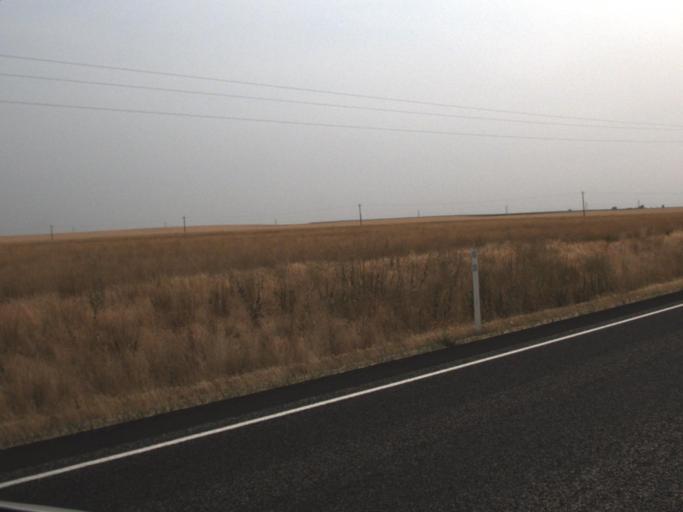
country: US
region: Washington
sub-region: Benton County
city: Benton City
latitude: 46.1340
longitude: -119.6015
